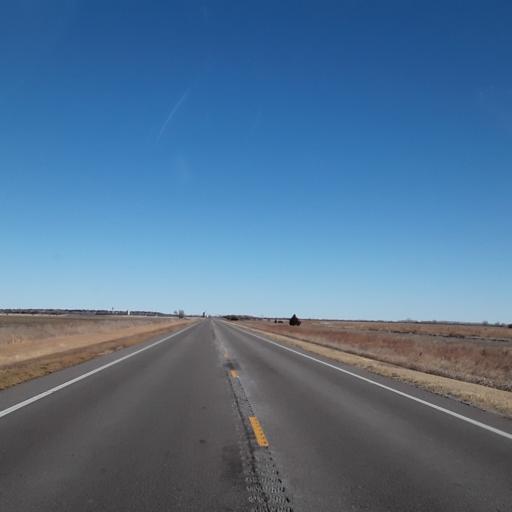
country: US
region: Kansas
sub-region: Pawnee County
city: Larned
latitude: 38.1404
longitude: -99.1499
